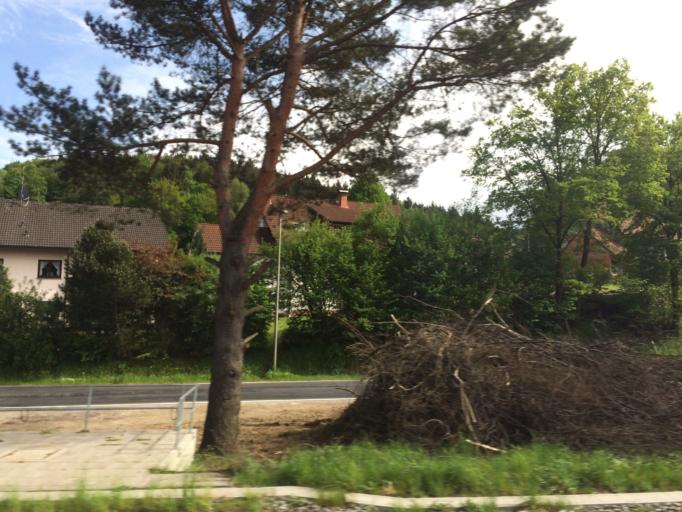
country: DE
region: Bavaria
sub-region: Regierungsbezirk Unterfranken
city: Wiesthal
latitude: 50.0183
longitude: 9.4468
